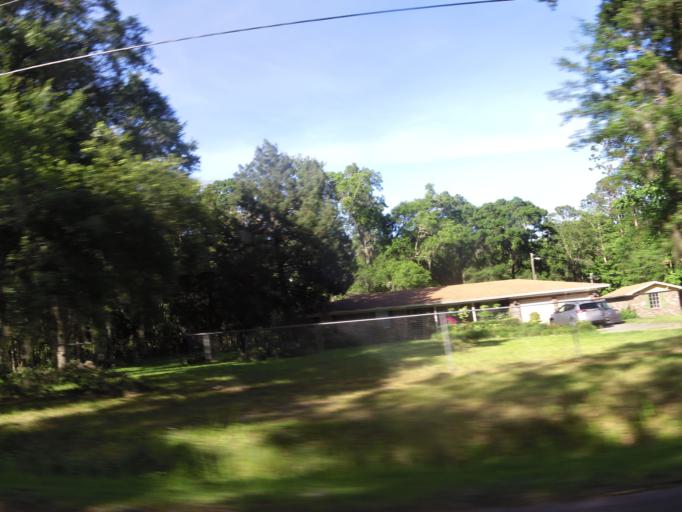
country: US
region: Florida
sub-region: Nassau County
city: Nassau Village-Ratliff
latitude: 30.4642
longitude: -81.8345
